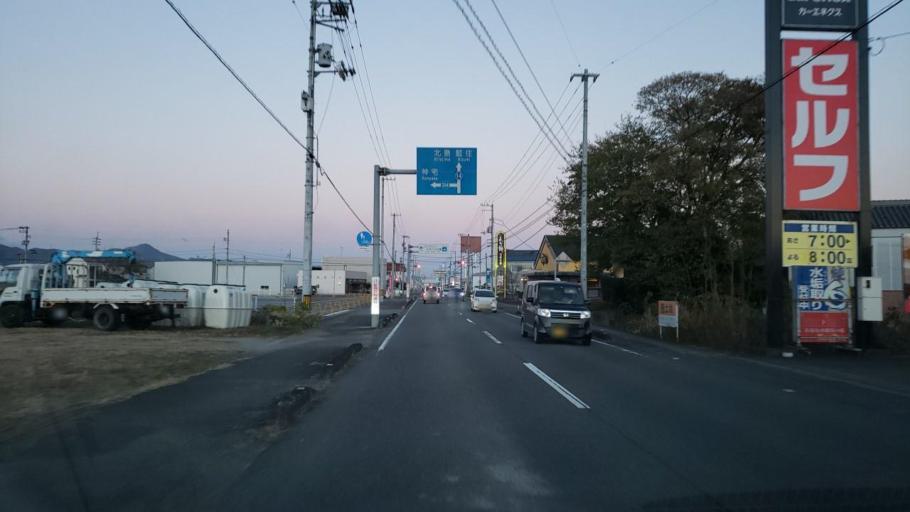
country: JP
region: Tokushima
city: Ishii
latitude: 34.1161
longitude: 134.4237
